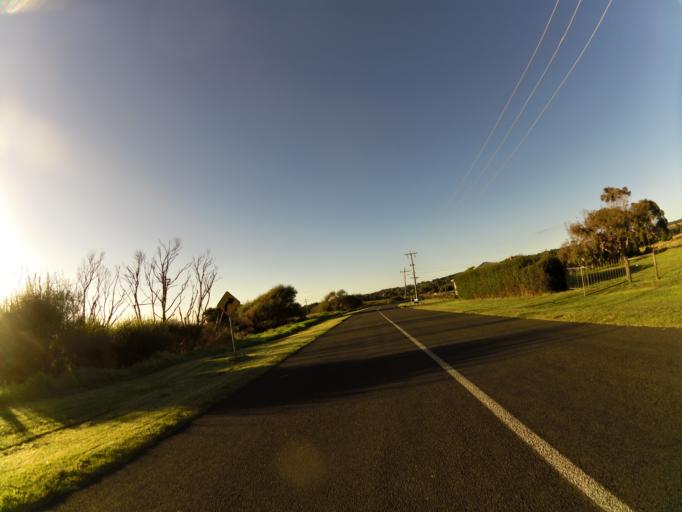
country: AU
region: Victoria
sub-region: Colac-Otway
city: Apollo Bay
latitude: -38.7650
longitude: 143.6610
